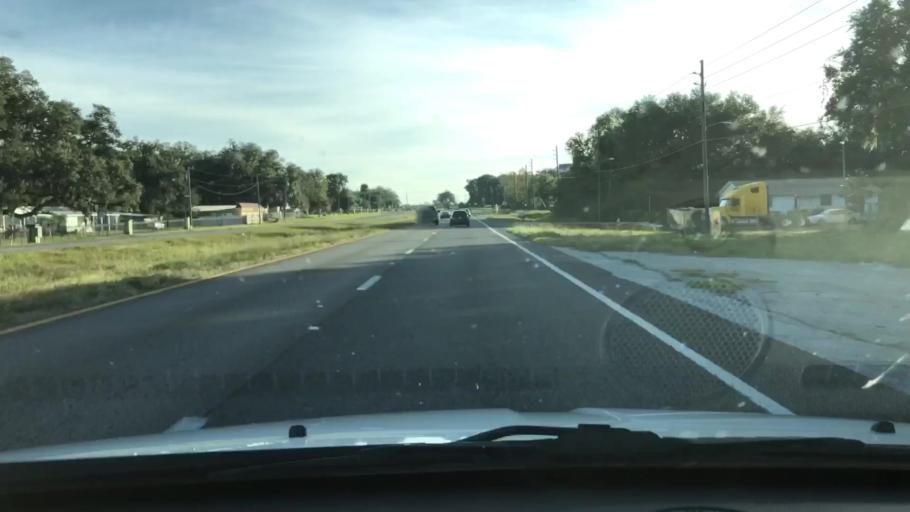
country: US
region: Florida
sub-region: Osceola County
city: Campbell
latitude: 28.2582
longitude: -81.4469
